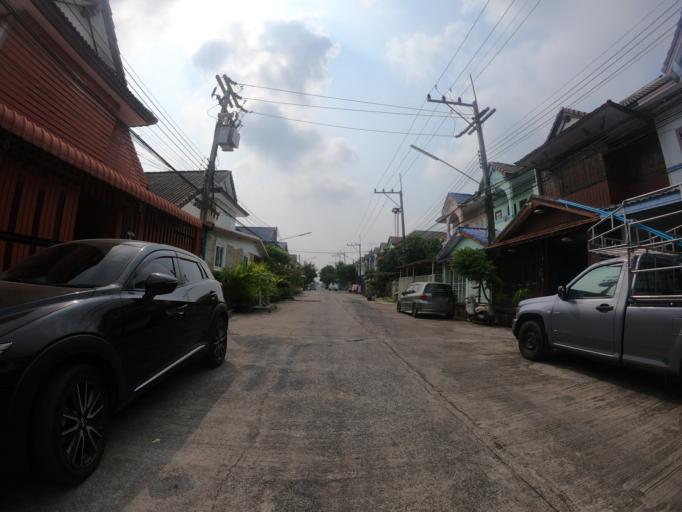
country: TH
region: Pathum Thani
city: Nong Suea
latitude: 14.0765
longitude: 100.8584
